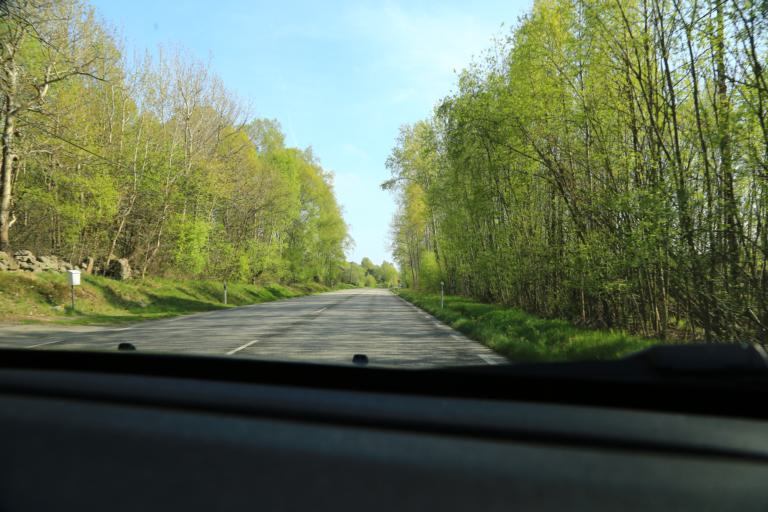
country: SE
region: Halland
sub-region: Varbergs Kommun
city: Varberg
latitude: 57.1783
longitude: 12.2274
